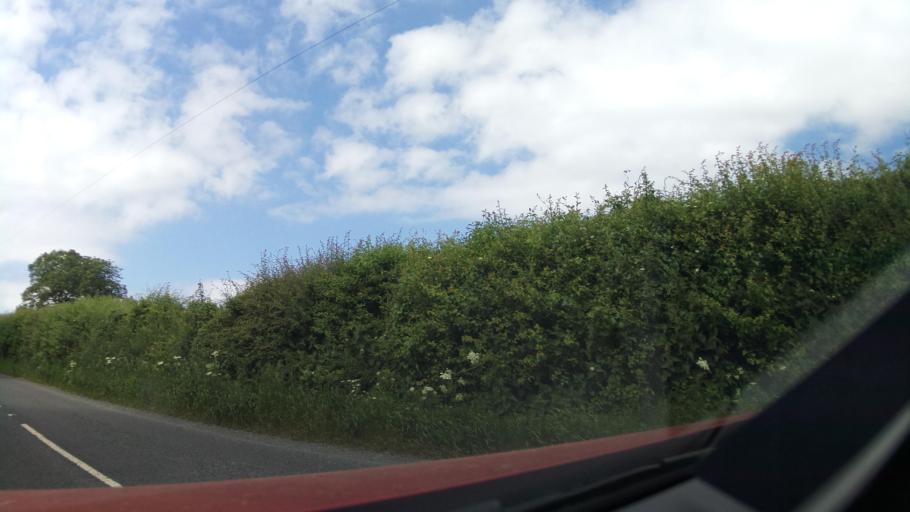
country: GB
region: England
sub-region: Somerset
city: Wincanton
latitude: 51.0307
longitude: -2.4554
